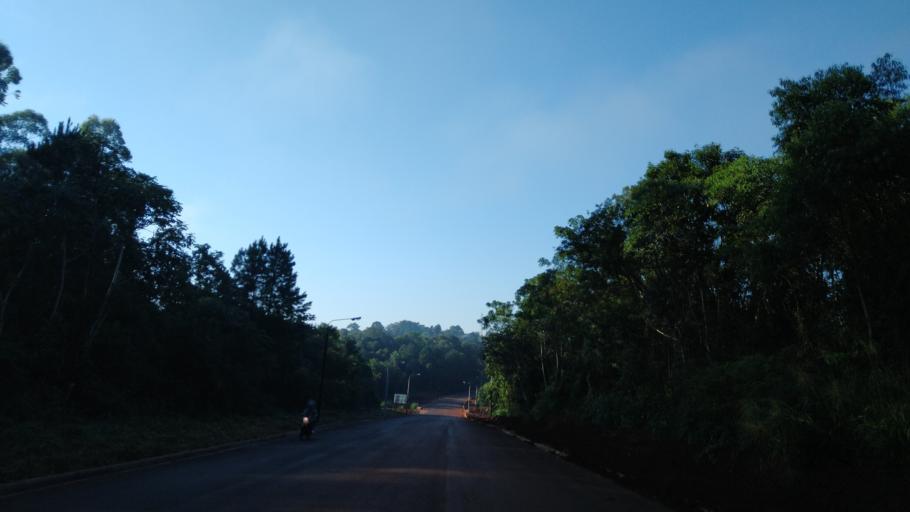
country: AR
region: Misiones
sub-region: Departamento de Montecarlo
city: Montecarlo
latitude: -26.5598
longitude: -54.7703
